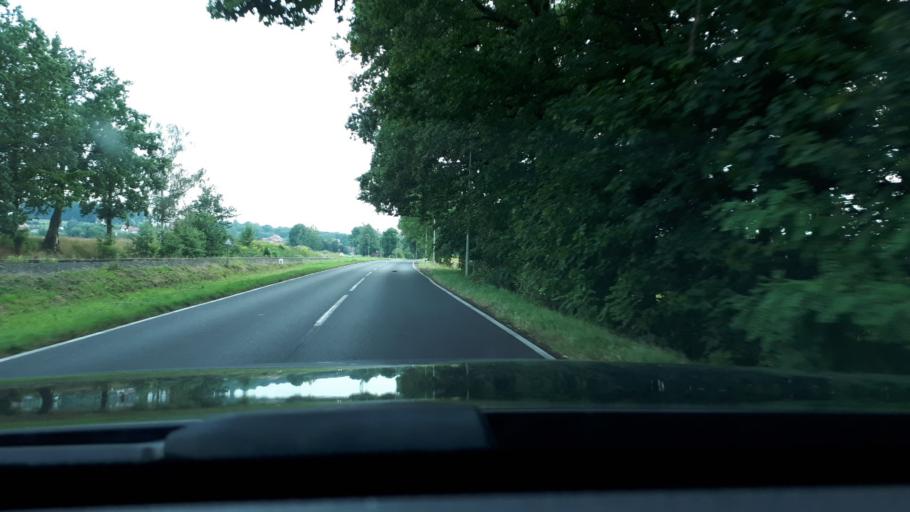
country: PL
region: Lower Silesian Voivodeship
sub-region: Powiat lubanski
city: Luban
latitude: 51.0735
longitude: 15.2938
